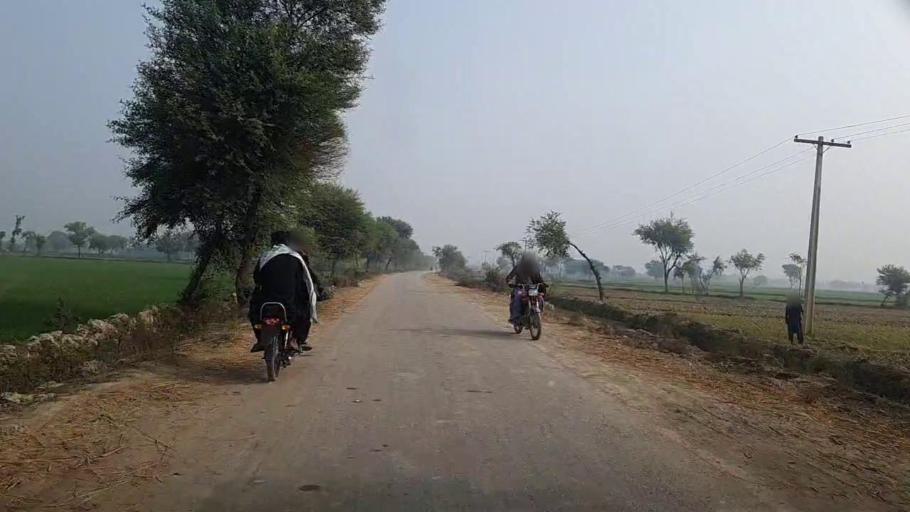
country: PK
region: Sindh
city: Dadu
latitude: 26.8327
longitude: 67.7692
